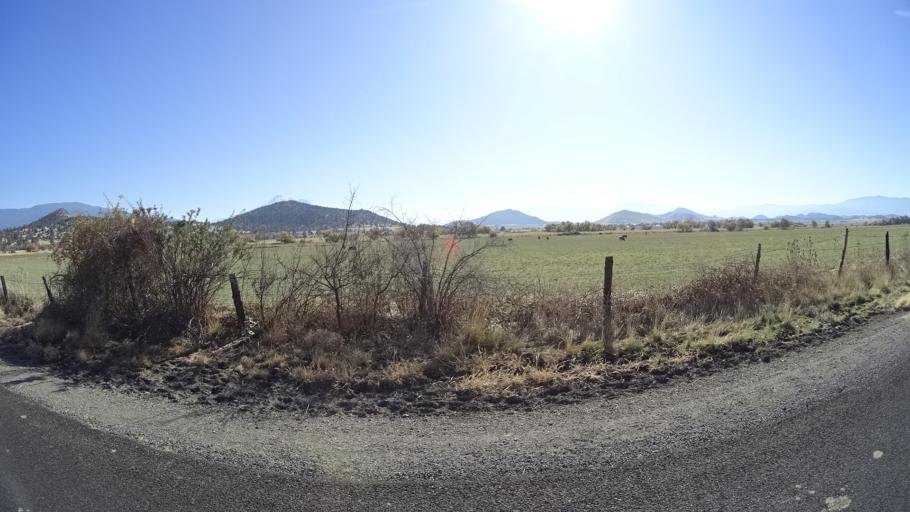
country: US
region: California
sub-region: Siskiyou County
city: Montague
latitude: 41.7263
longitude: -122.3794
